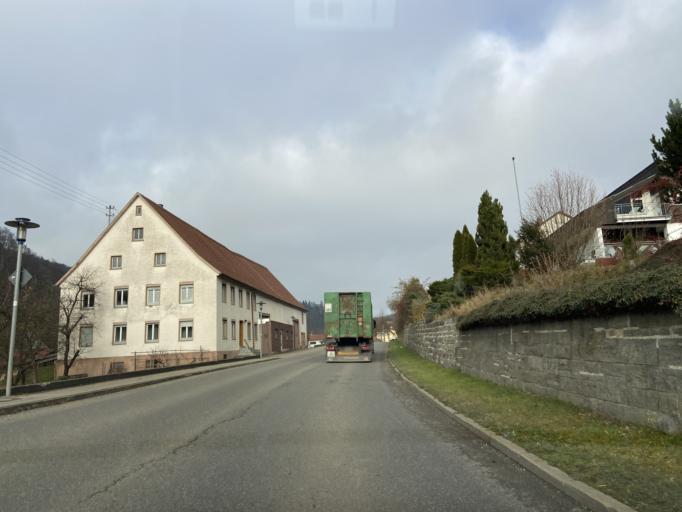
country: DE
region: Baden-Wuerttemberg
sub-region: Tuebingen Region
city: Hettingen
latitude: 48.2122
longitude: 9.2304
